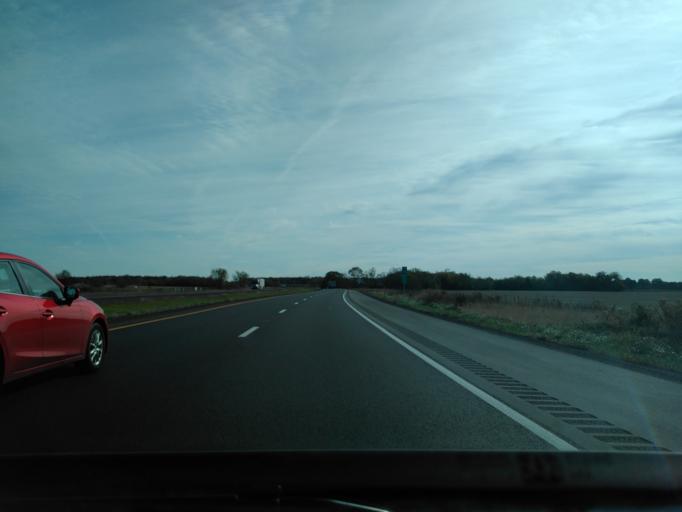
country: US
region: Illinois
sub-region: Madison County
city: Highland
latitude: 38.7872
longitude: -89.6837
